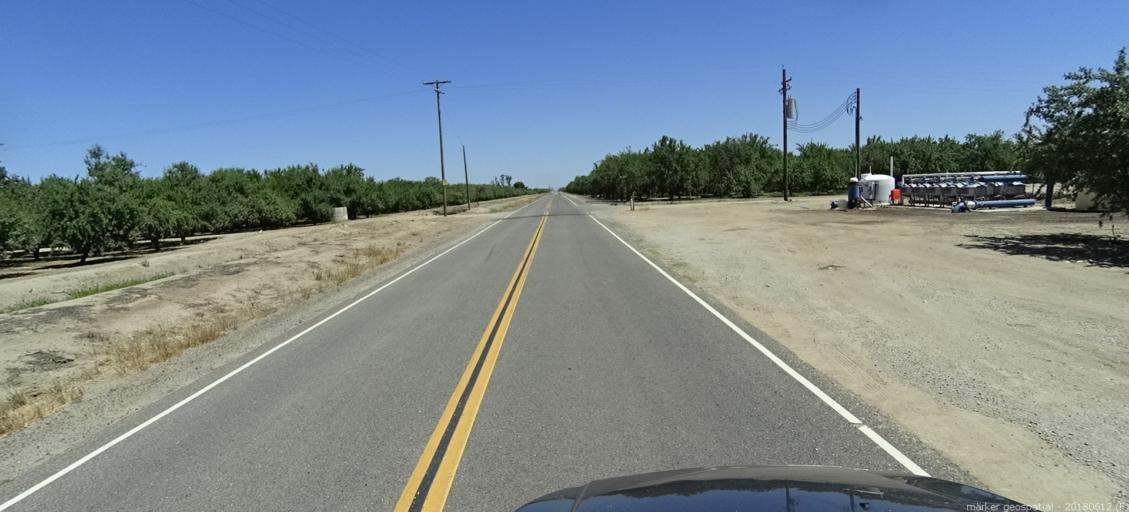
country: US
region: California
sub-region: Madera County
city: Chowchilla
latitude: 37.0611
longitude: -120.3830
